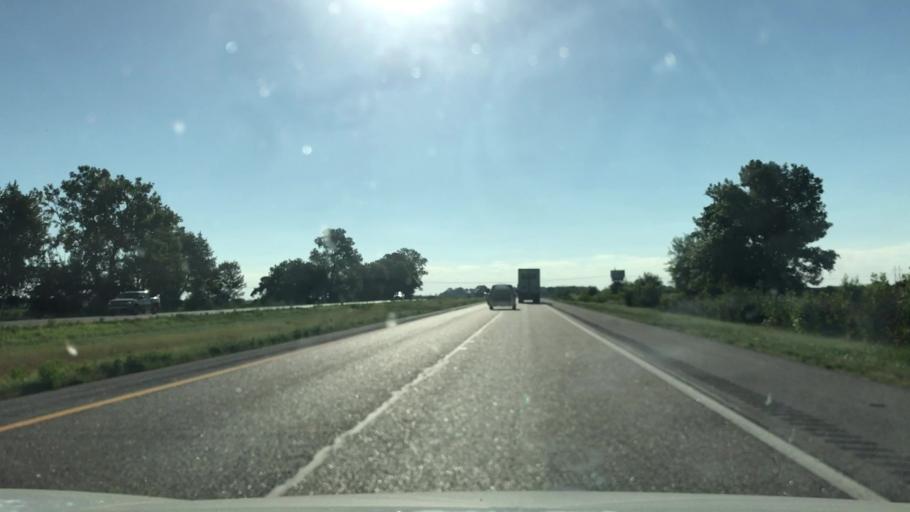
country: US
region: Illinois
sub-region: Saint Clair County
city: Lebanon
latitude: 38.5506
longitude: -89.7921
